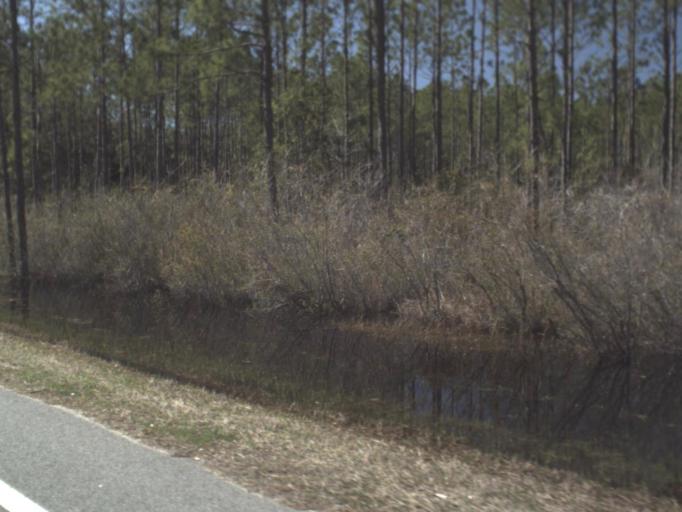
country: US
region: Florida
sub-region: Bay County
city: Panama City Beach
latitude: 30.3183
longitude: -85.8051
